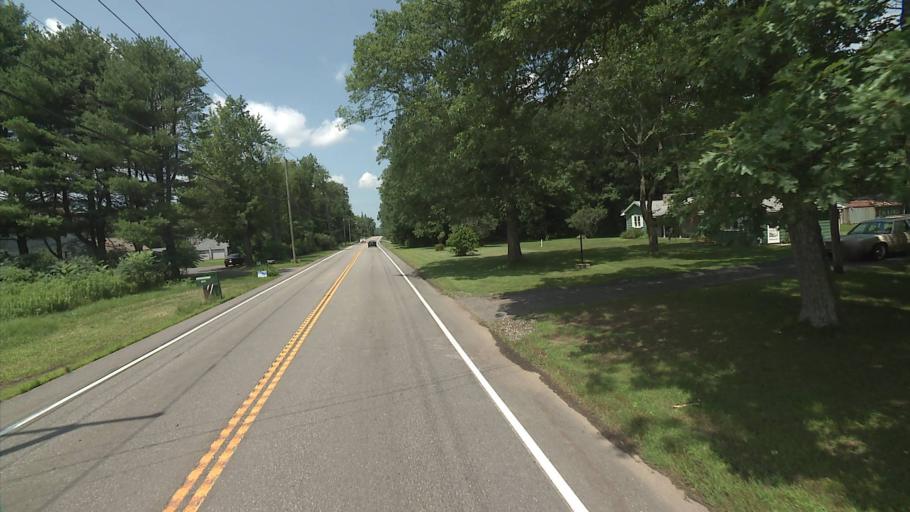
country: US
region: Connecticut
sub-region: Tolland County
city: Tolland
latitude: 41.8186
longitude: -72.3972
